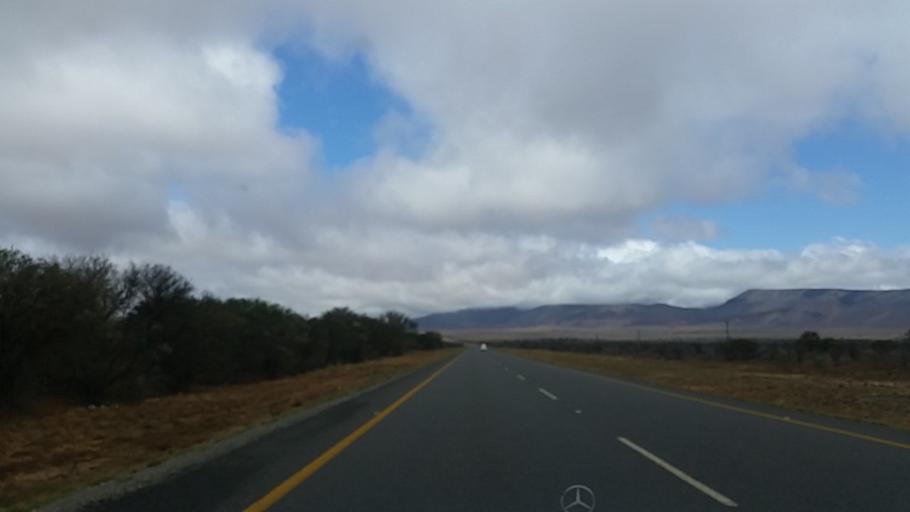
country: ZA
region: Eastern Cape
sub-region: Cacadu District Municipality
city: Graaff-Reinet
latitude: -31.9956
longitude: 24.6757
